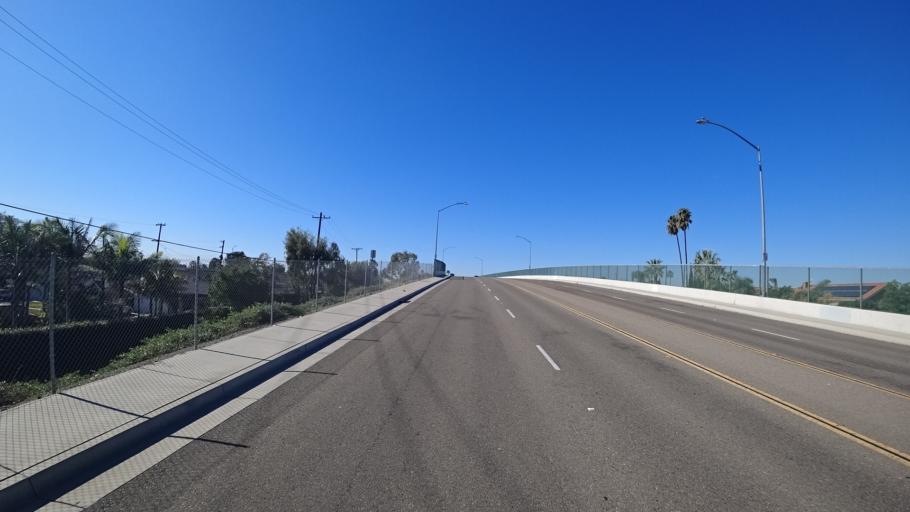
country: US
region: California
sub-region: Orange County
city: Orange
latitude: 33.7808
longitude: -117.8299
